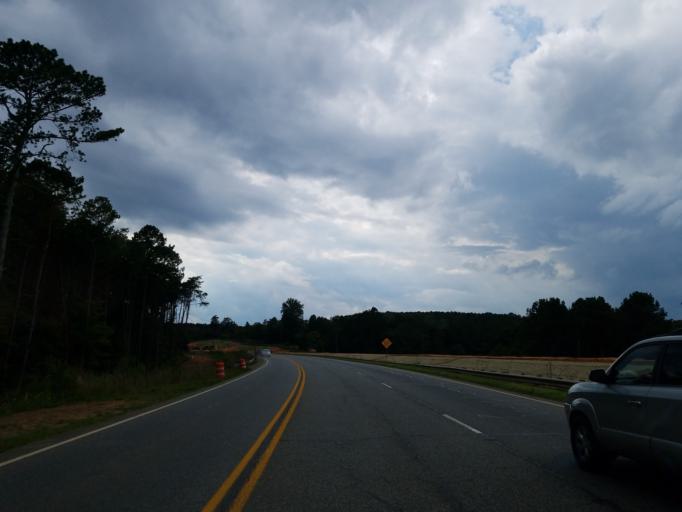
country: US
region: Georgia
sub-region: Bartow County
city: Adairsville
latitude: 34.3730
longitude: -84.9811
